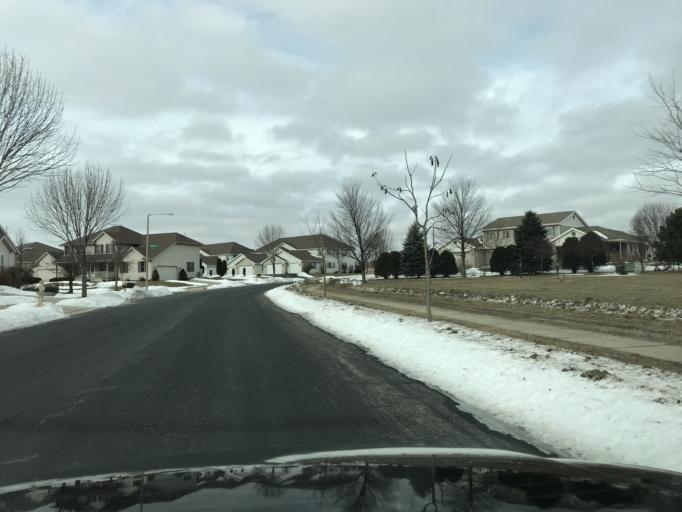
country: US
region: Wisconsin
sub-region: Dane County
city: Cottage Grove
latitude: 43.0974
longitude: -89.2631
